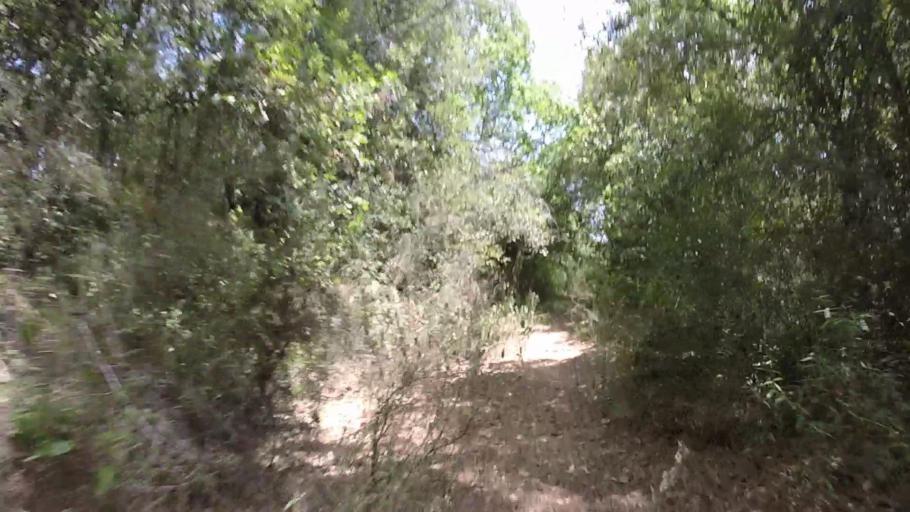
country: FR
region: Provence-Alpes-Cote d'Azur
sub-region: Departement des Alpes-Maritimes
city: Mougins
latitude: 43.6138
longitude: 7.0310
